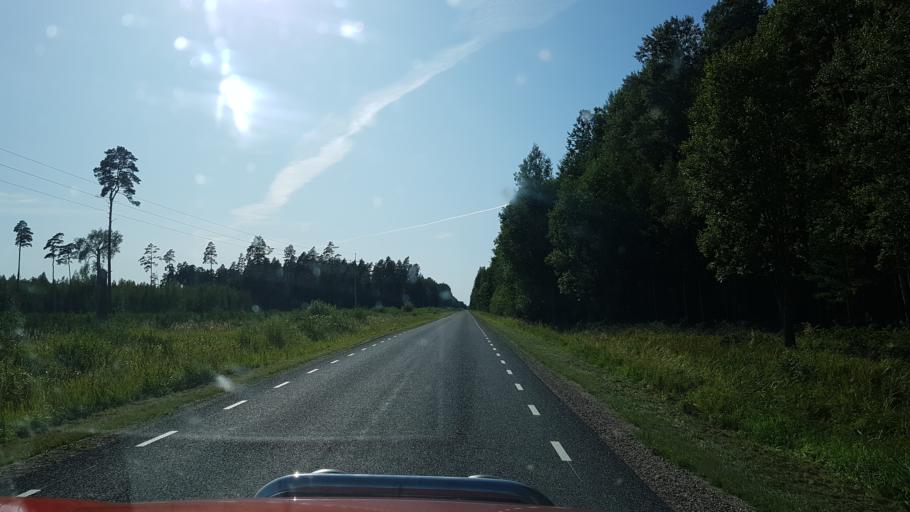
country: LV
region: Aloja
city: Staicele
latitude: 58.0856
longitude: 24.5999
